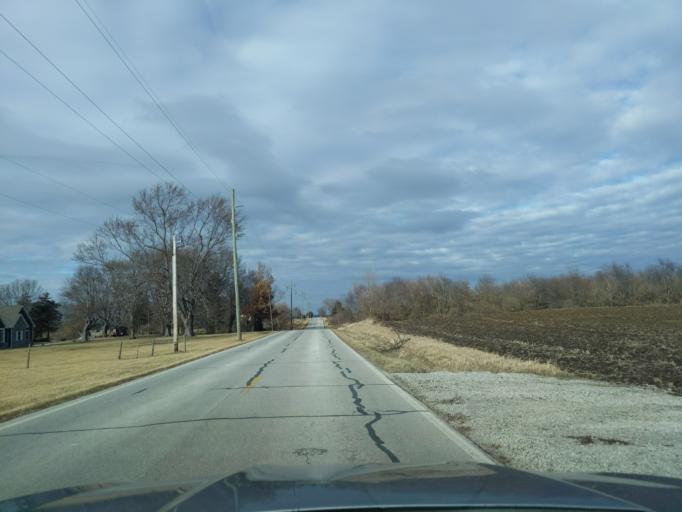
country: US
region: Indiana
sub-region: Tippecanoe County
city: Shadeland
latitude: 40.3458
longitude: -86.9755
